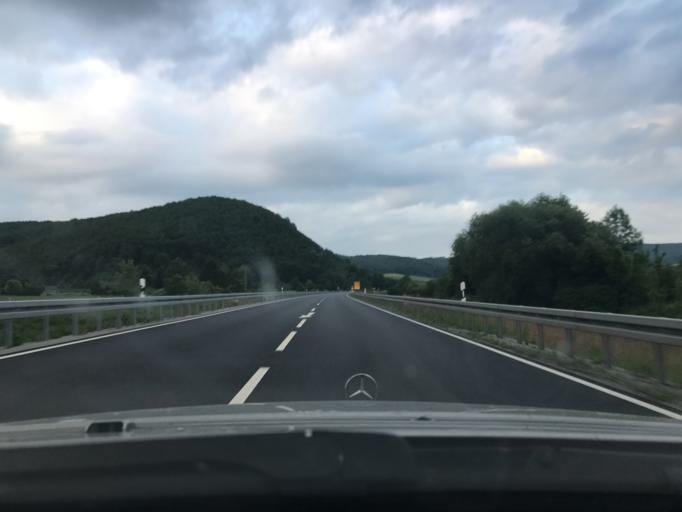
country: DE
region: Hesse
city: Wanfried
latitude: 51.1892
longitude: 10.1300
